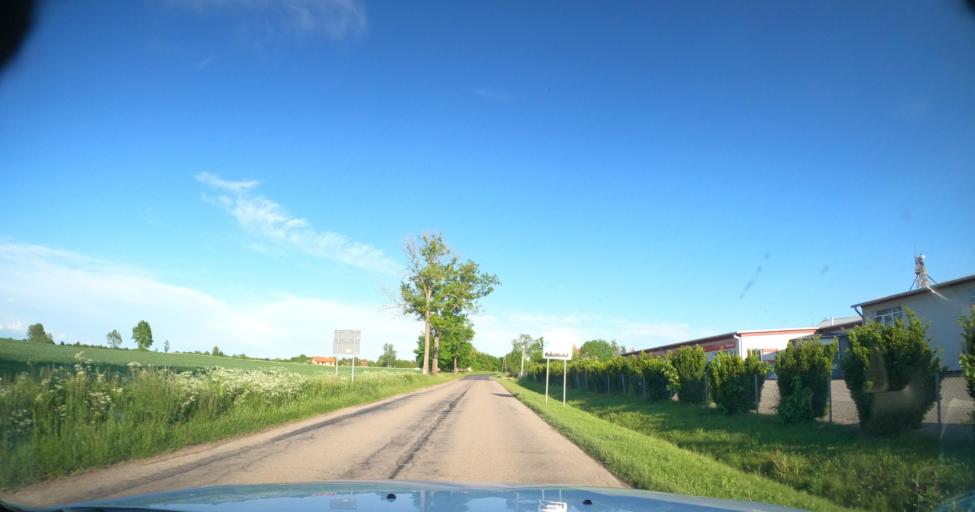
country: PL
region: Warmian-Masurian Voivodeship
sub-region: Powiat braniewski
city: Braniewo
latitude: 54.2741
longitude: 19.9310
